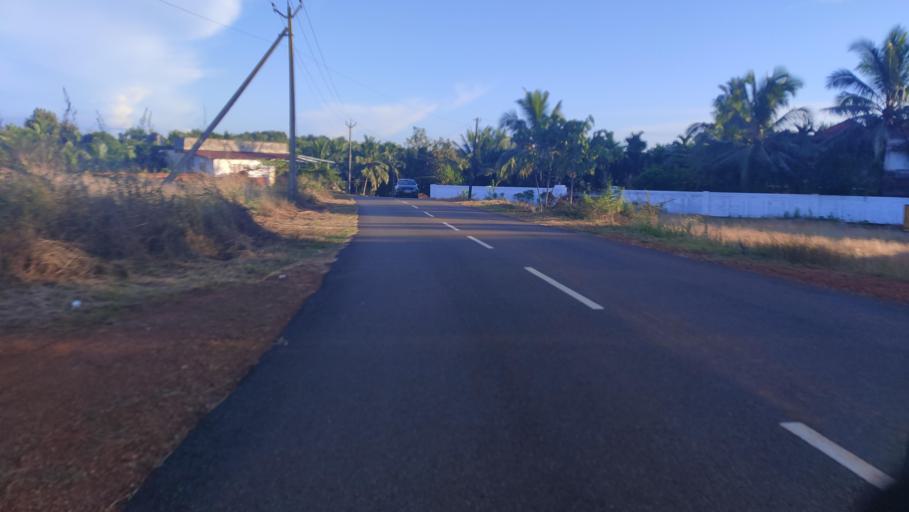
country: IN
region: Kerala
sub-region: Kasaragod District
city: Kasaragod
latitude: 12.4550
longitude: 75.0969
